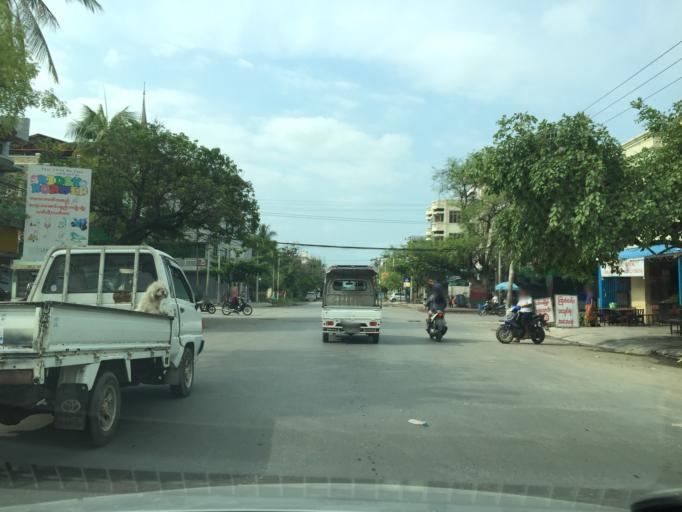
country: MM
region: Mandalay
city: Mandalay
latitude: 21.9729
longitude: 96.0806
